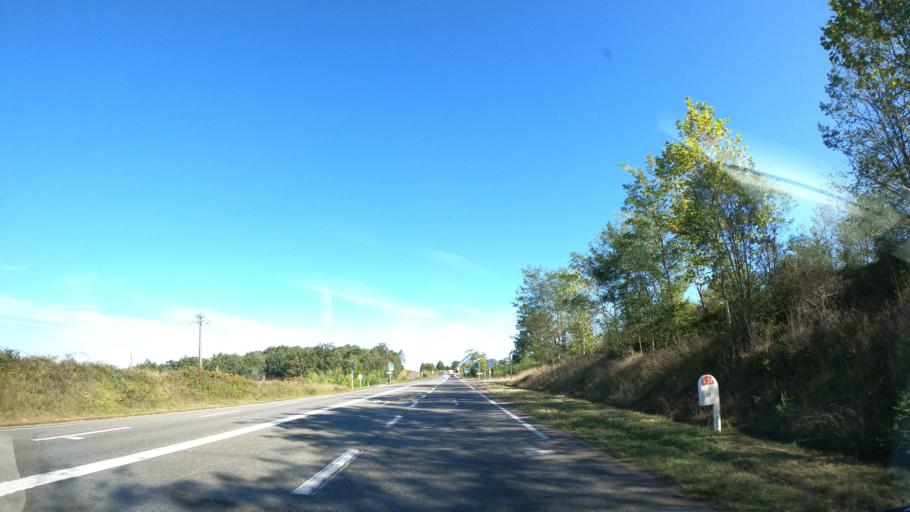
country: FR
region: Aquitaine
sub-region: Departement de la Dordogne
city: Vergt
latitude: 45.0077
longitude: 0.6044
